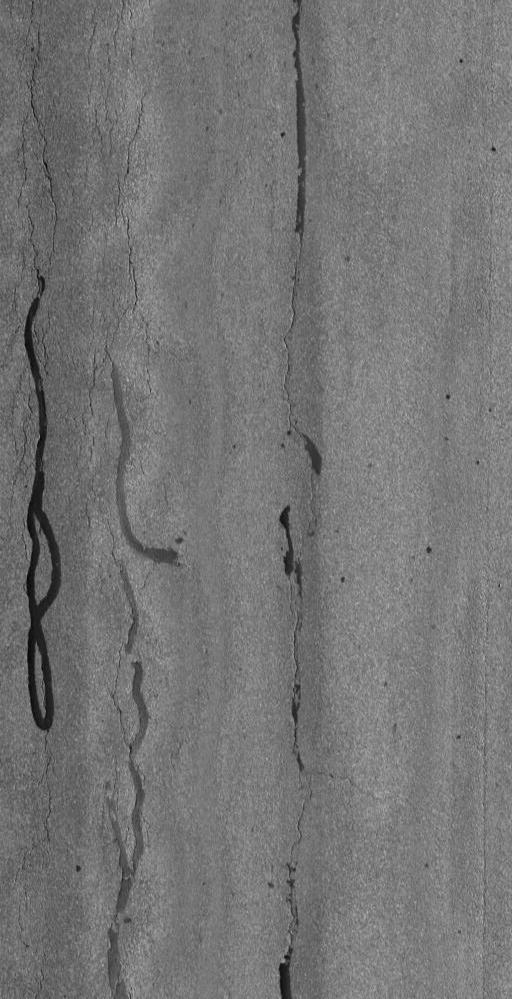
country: US
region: Vermont
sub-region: Chittenden County
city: Burlington
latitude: 44.5175
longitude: -73.2593
